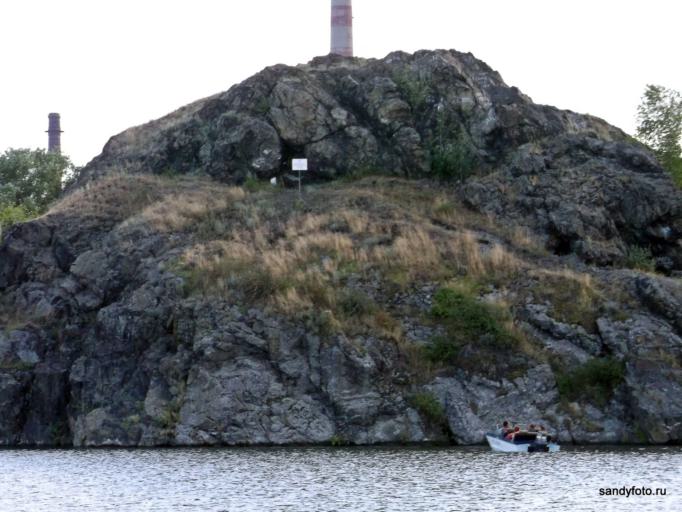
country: RU
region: Chelyabinsk
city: Troitsk
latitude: 54.0721
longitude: 61.5812
